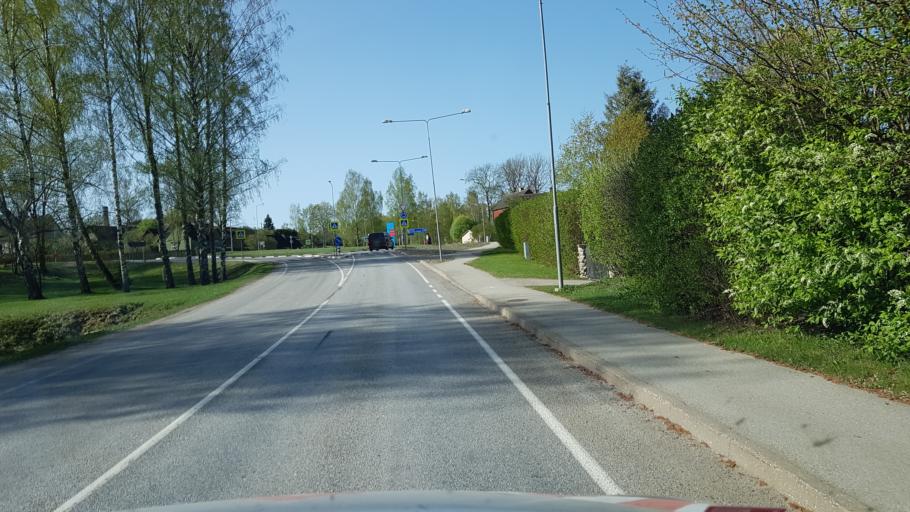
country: EE
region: Viljandimaa
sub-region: Abja vald
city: Abja-Paluoja
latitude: 58.1269
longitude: 25.3601
